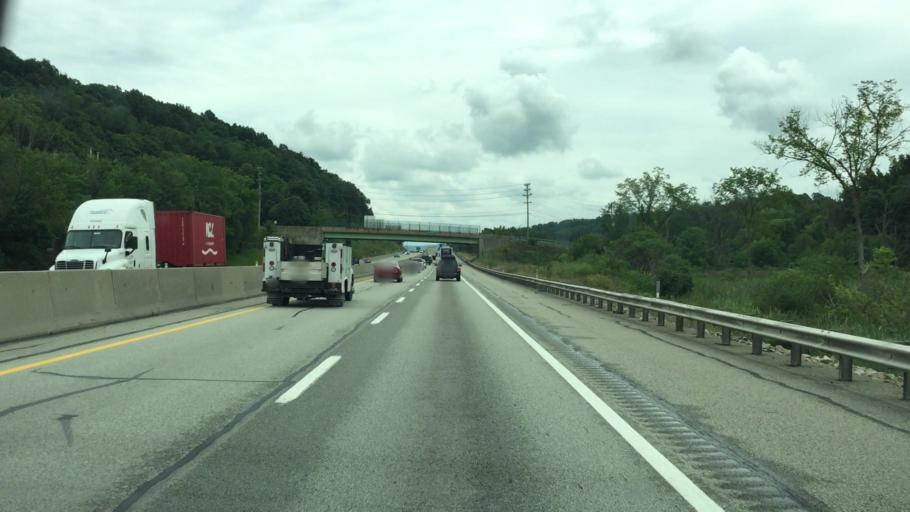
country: US
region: Pennsylvania
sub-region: Westmoreland County
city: Youngwood
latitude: 40.2111
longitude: -79.5797
